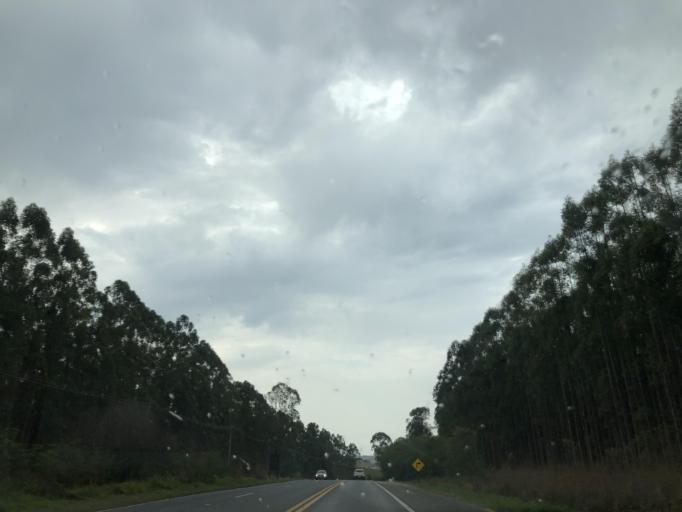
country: BR
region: Sao Paulo
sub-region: Salto De Pirapora
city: Salto de Pirapora
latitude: -23.6672
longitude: -47.5999
